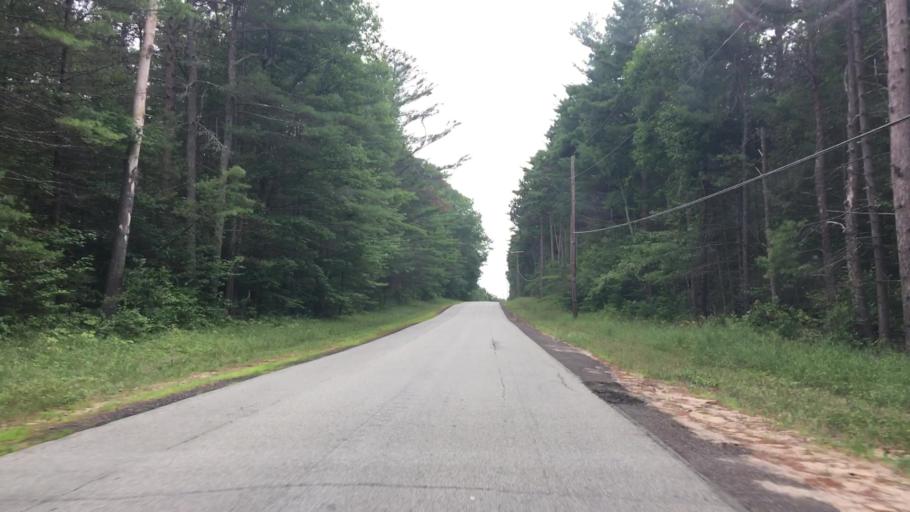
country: US
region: New York
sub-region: Essex County
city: Keeseville
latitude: 44.4595
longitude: -73.5775
